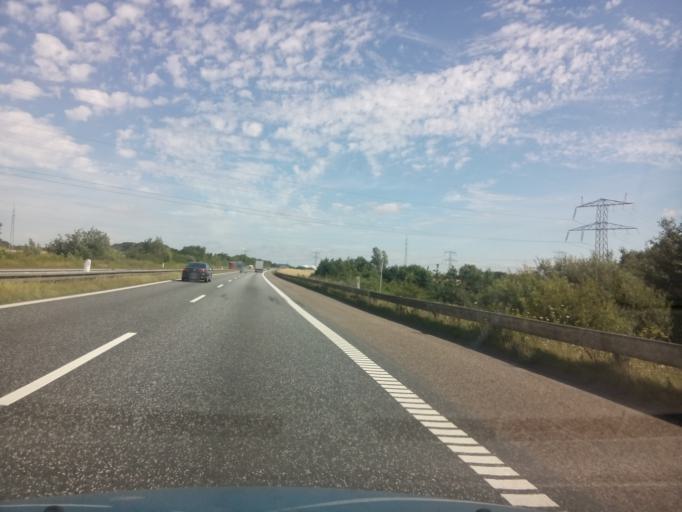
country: DK
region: Central Jutland
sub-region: Arhus Kommune
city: Trige
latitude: 56.2716
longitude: 10.1310
